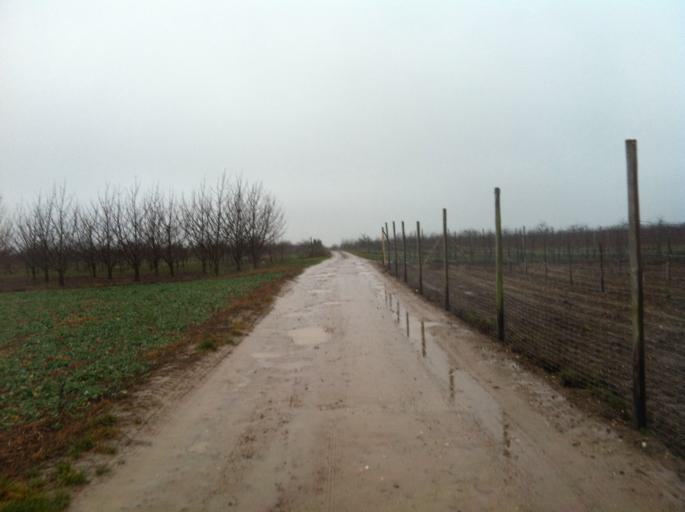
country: DE
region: Rheinland-Pfalz
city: Wackernheim
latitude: 49.9837
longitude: 8.1407
